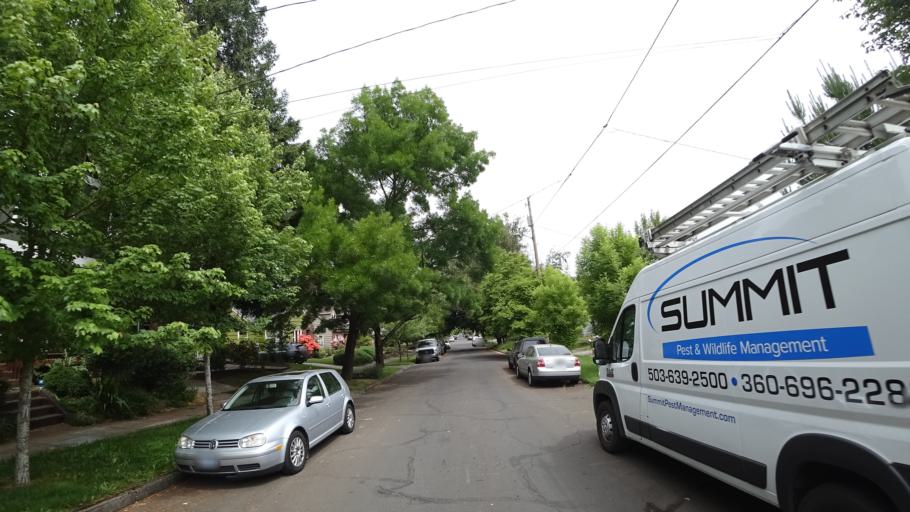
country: US
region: Oregon
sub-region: Multnomah County
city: Portland
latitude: 45.5653
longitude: -122.6414
